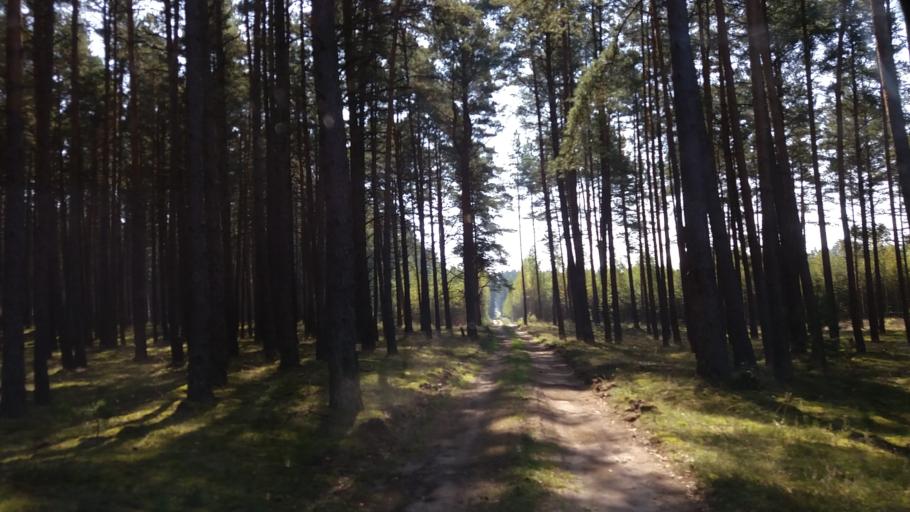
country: PL
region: West Pomeranian Voivodeship
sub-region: Powiat drawski
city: Kalisz Pomorski
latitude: 53.1947
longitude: 15.8962
